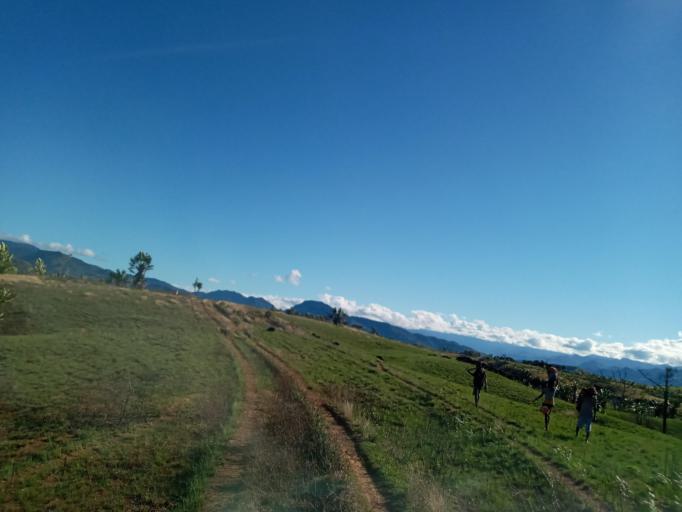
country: MG
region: Anosy
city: Fort Dauphin
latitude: -24.4056
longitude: 47.2499
